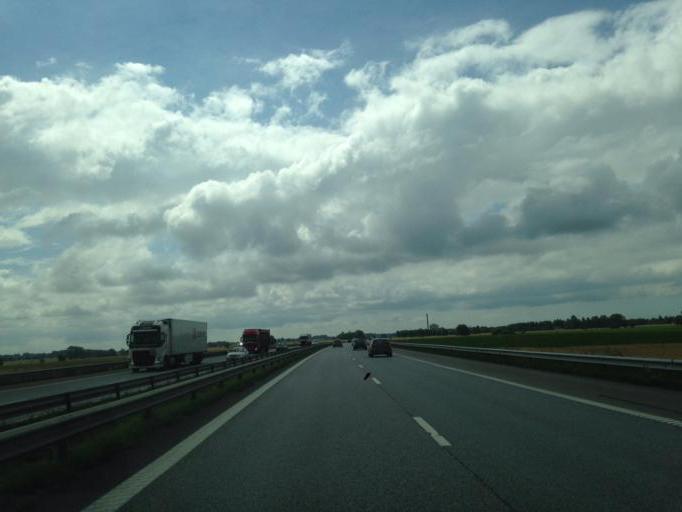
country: SE
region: Skane
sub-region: Lomma Kommun
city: Lomma
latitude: 55.7045
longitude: 13.0973
